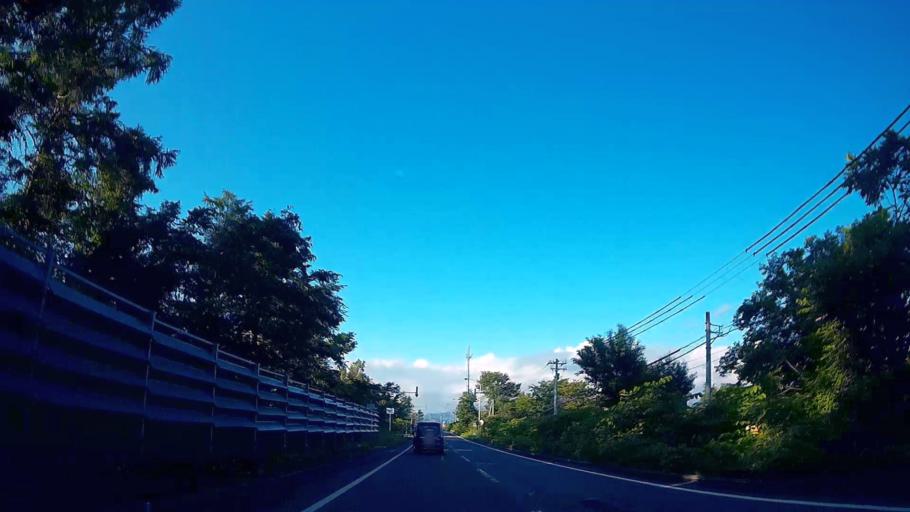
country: JP
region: Hokkaido
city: Date
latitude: 42.6237
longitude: 140.7964
